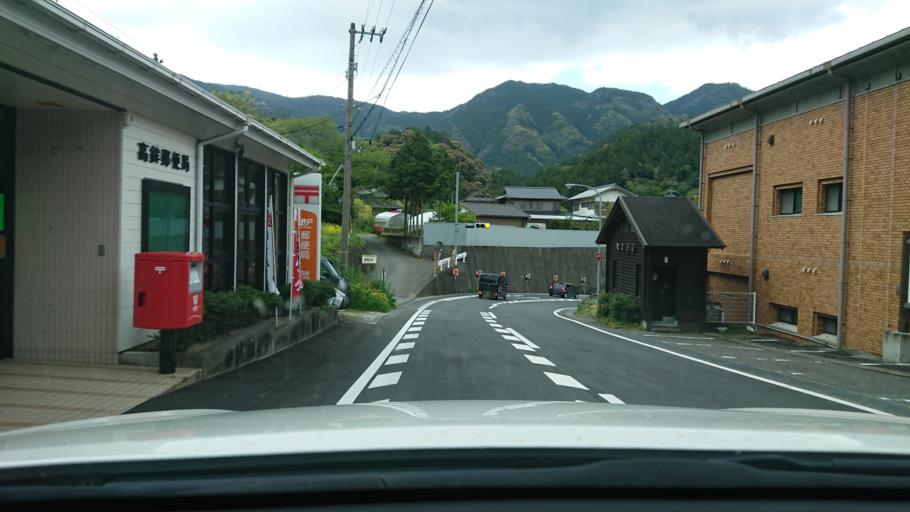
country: JP
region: Tokushima
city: Ishii
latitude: 33.9202
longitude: 134.4261
